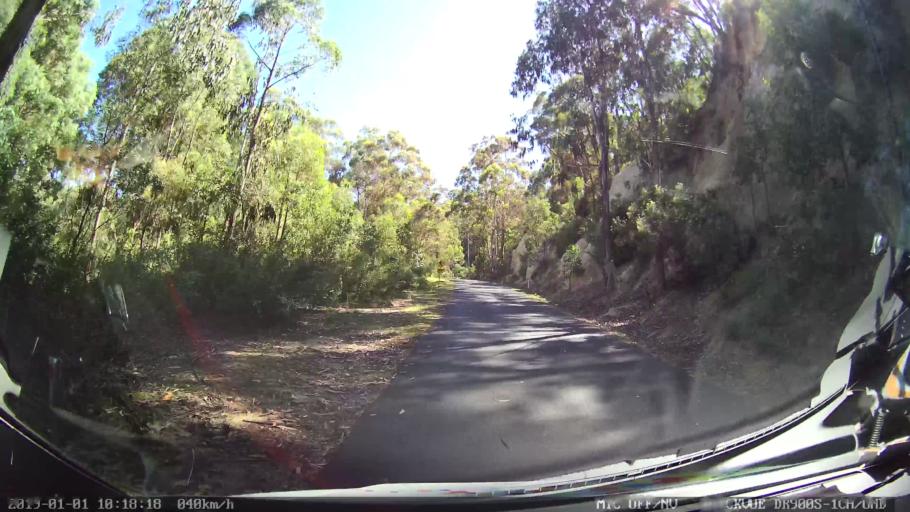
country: AU
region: New South Wales
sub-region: Snowy River
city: Jindabyne
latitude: -36.0893
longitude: 148.1815
